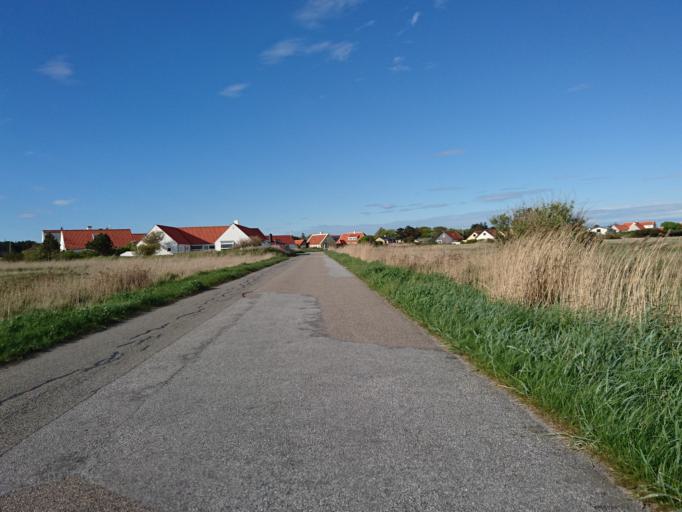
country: DK
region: North Denmark
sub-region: Frederikshavn Kommune
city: Skagen
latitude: 57.7135
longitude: 10.5654
